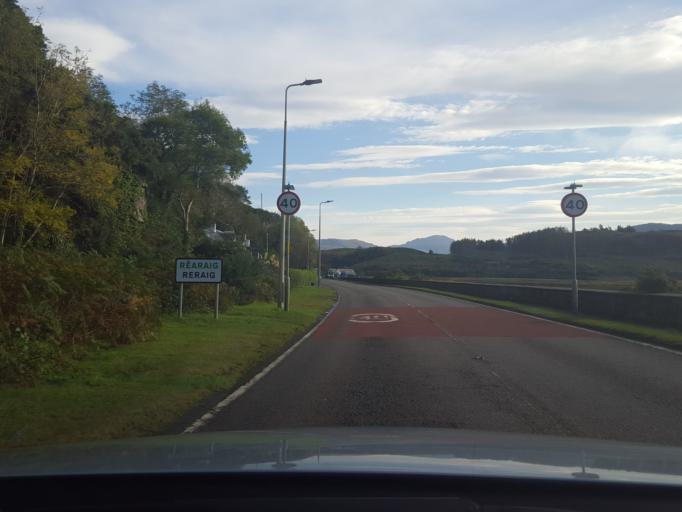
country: GB
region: Scotland
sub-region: Highland
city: Portree
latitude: 57.2826
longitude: -5.6333
